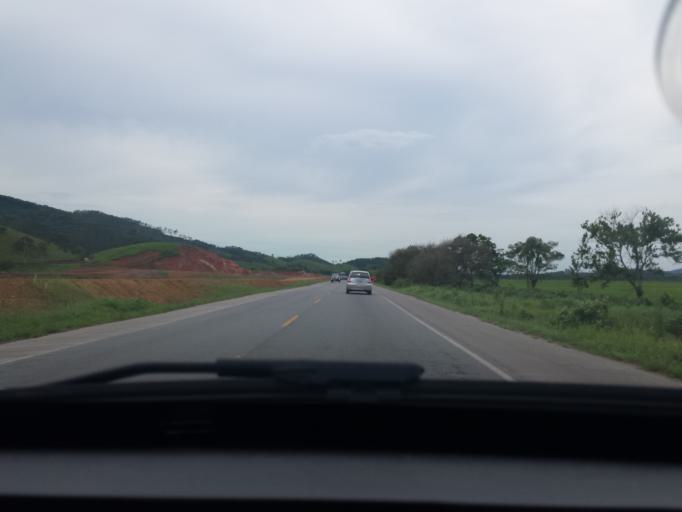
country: BR
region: Santa Catarina
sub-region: Gaspar
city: Gaspar
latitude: -26.8857
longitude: -48.8709
